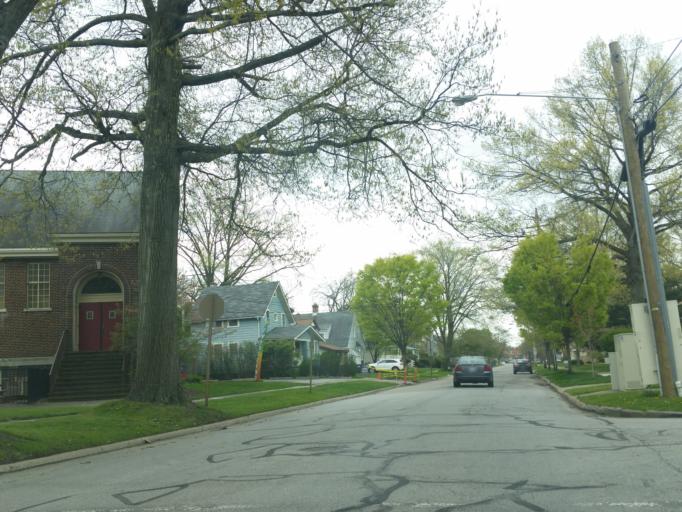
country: US
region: Ohio
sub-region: Cuyahoga County
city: Lakewood
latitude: 41.4734
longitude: -81.8004
